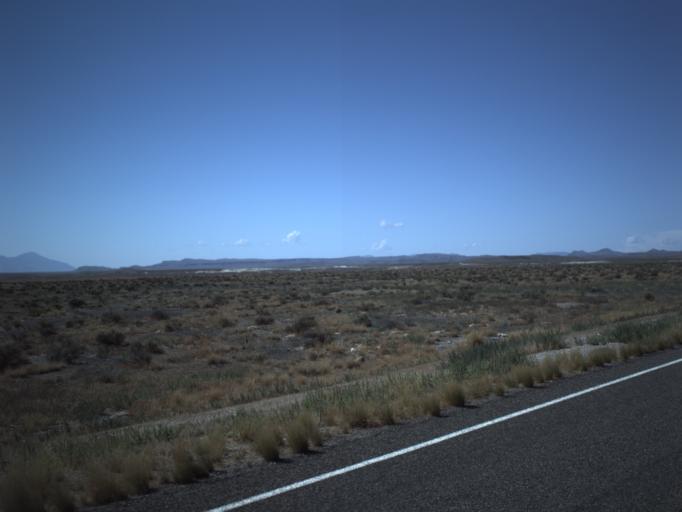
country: US
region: Utah
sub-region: Millard County
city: Delta
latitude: 39.0745
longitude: -113.2119
